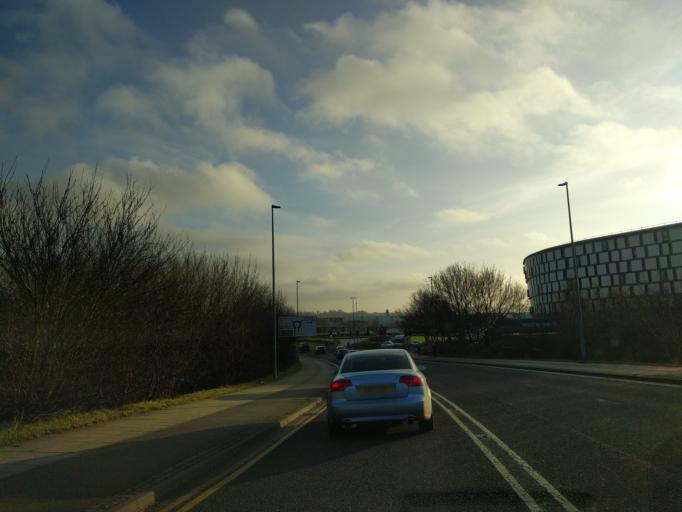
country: GB
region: England
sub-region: Lincolnshire
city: Lincoln
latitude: 53.2279
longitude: -0.5509
